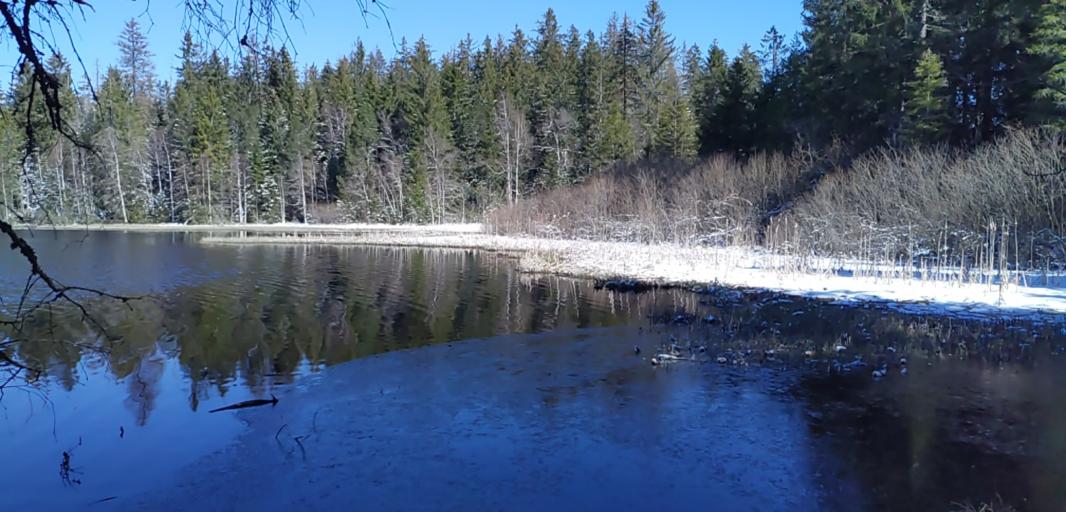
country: CH
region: Bern
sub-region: Jura bernois
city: Tramelan
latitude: 47.2387
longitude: 7.0523
